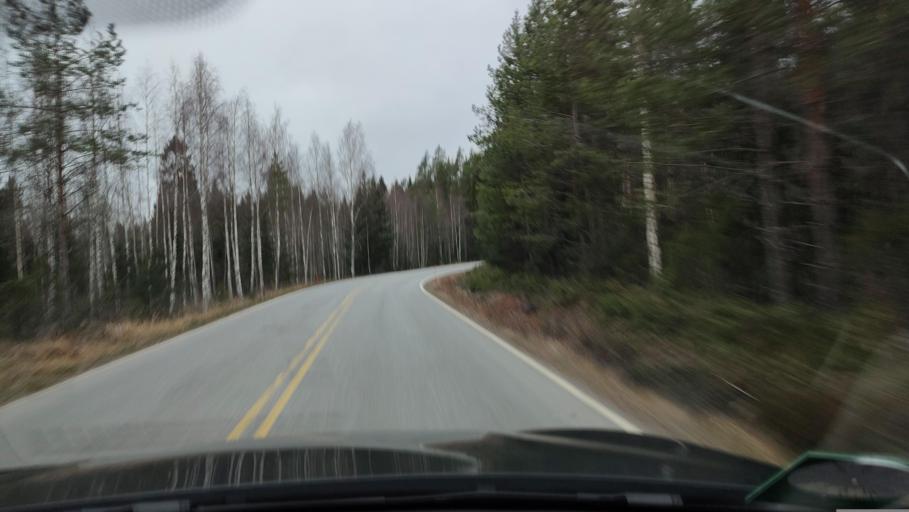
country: FI
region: Southern Ostrobothnia
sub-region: Suupohja
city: Karijoki
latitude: 62.2446
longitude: 21.7573
